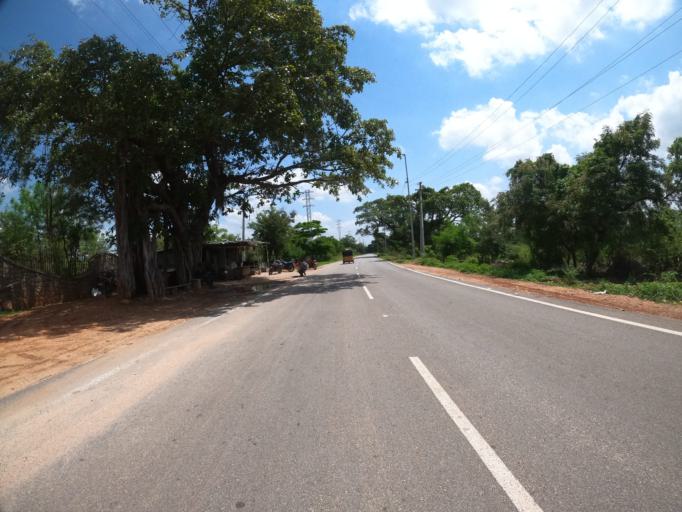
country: IN
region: Telangana
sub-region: Rangareddi
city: Sriramnagar
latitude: 17.3585
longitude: 78.3227
